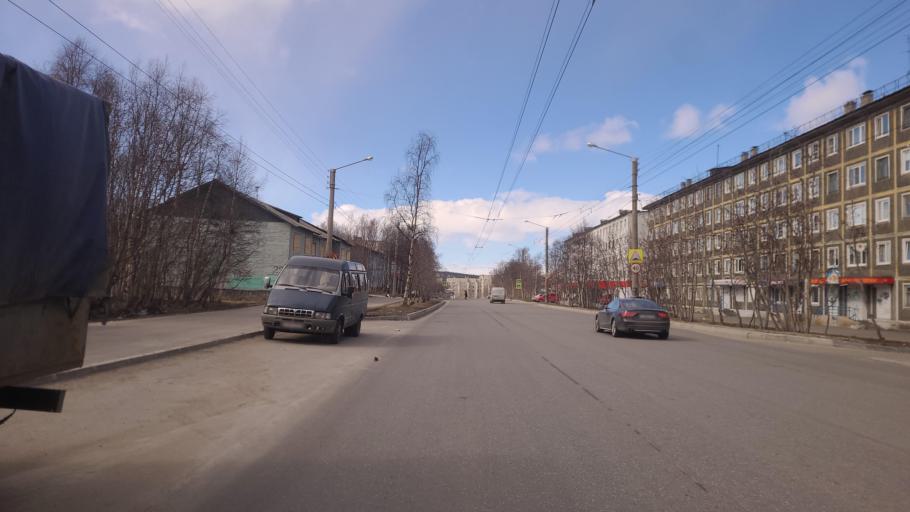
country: RU
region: Murmansk
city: Murmansk
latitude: 68.9523
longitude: 33.0719
